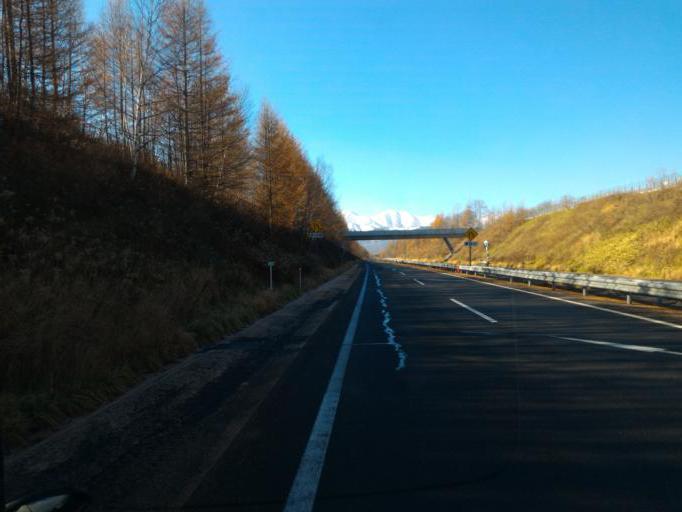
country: JP
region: Hokkaido
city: Otofuke
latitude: 42.9756
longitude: 142.9178
